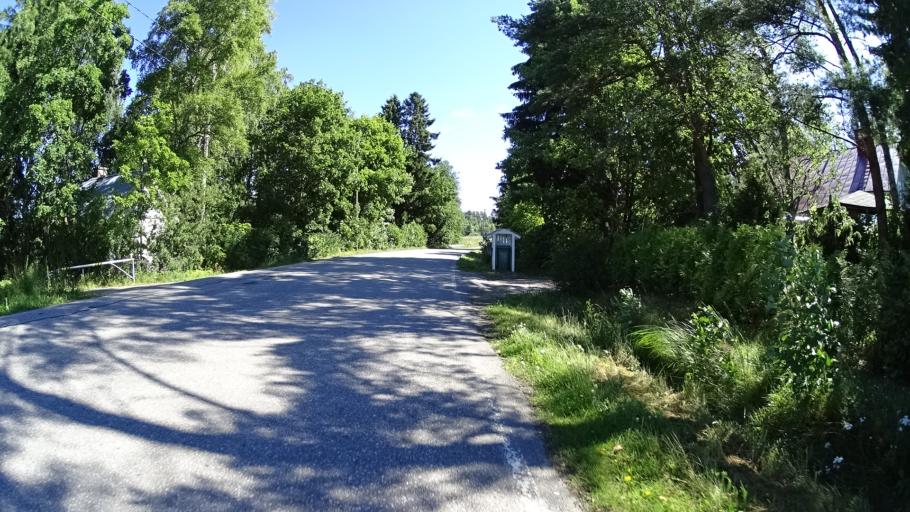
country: FI
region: Uusimaa
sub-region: Helsinki
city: Jaervenpaeae
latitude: 60.4431
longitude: 25.0731
